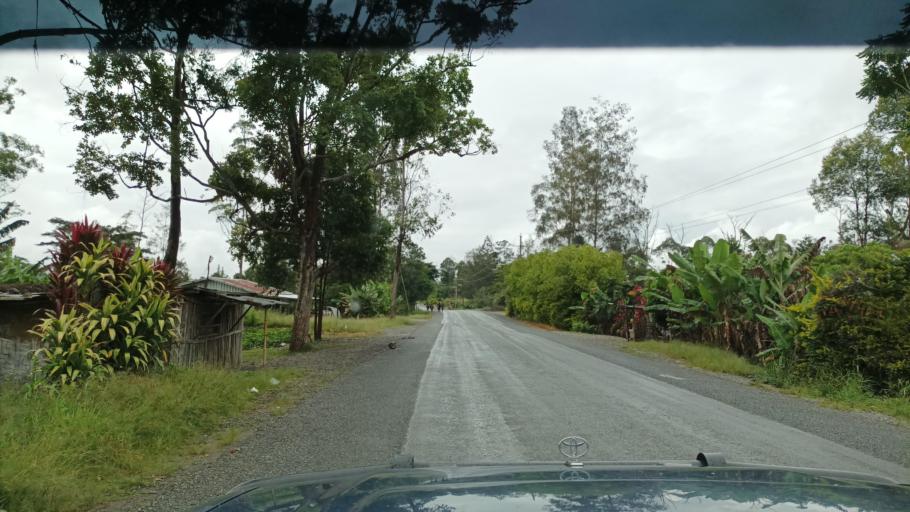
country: PG
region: Jiwaka
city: Minj
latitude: -5.8553
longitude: 144.6308
